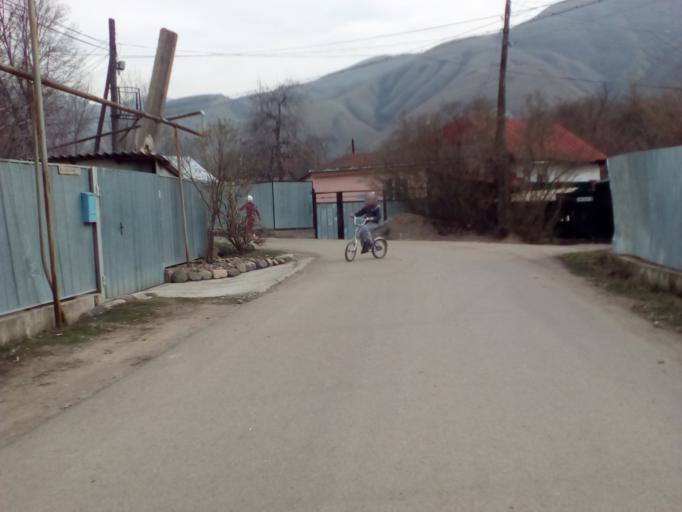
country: KZ
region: Almaty Oblysy
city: Burunday
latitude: 43.1579
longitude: 76.4098
